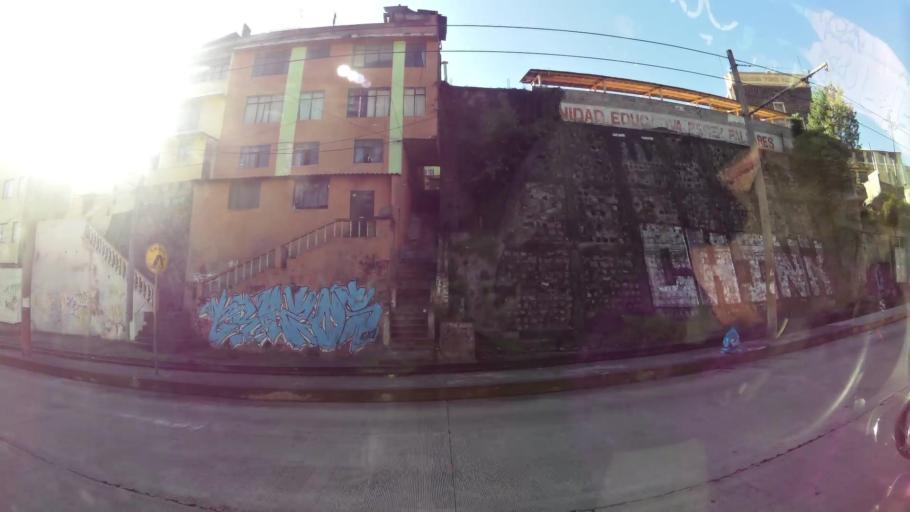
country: EC
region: Pichincha
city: Quito
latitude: -0.2415
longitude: -78.5176
